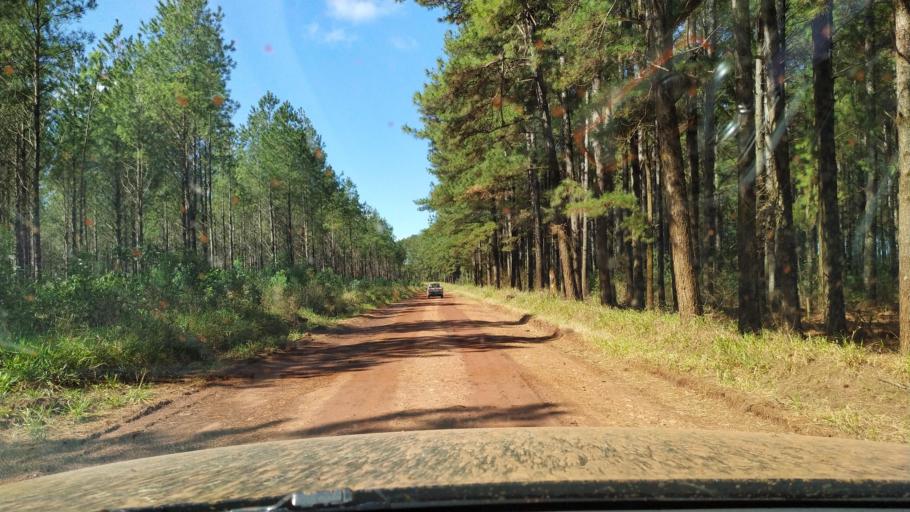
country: AR
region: Corrientes
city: Santo Tome
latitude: -28.3990
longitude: -56.0180
